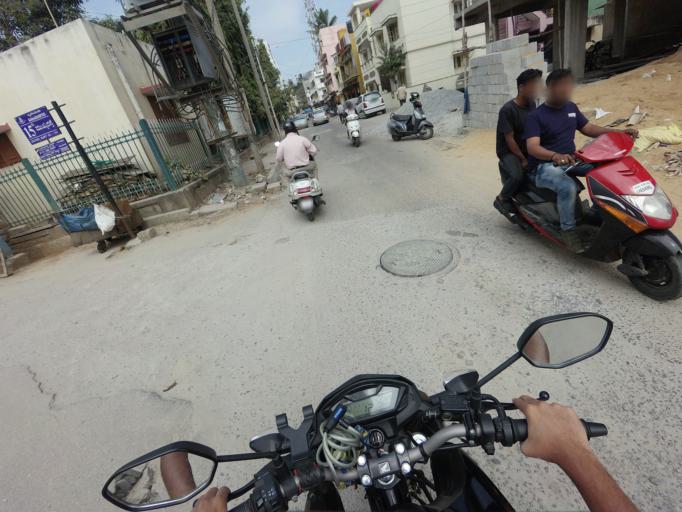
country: IN
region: Karnataka
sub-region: Bangalore Urban
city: Bangalore
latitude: 12.9690
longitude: 77.5403
